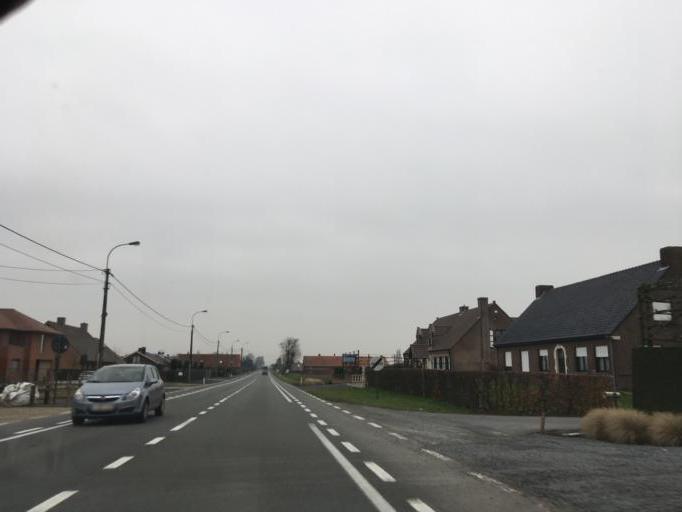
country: BE
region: Flanders
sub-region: Provincie West-Vlaanderen
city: Ingelmunster
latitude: 50.9532
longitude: 3.2462
